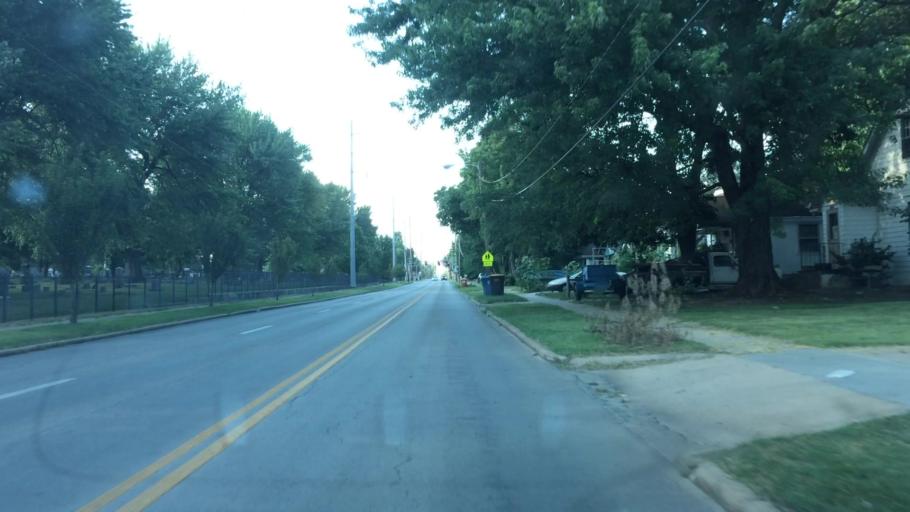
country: US
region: Missouri
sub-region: Greene County
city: Springfield
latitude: 37.1945
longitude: -93.2902
